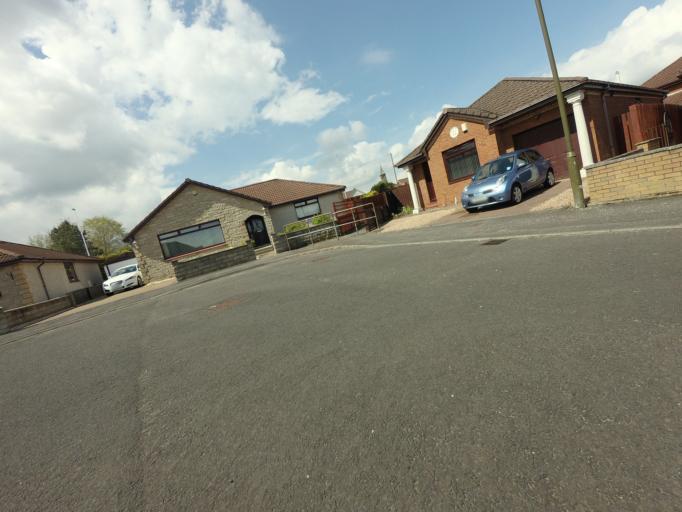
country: GB
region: Scotland
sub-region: Falkirk
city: Falkirk
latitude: 56.0220
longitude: -3.7926
